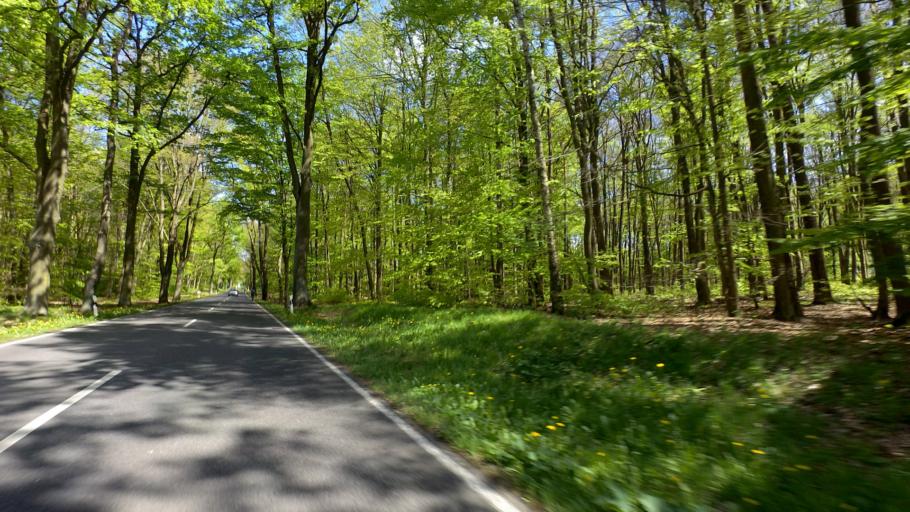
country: DE
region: Berlin
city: Blankenfelde
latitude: 52.6782
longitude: 13.4151
